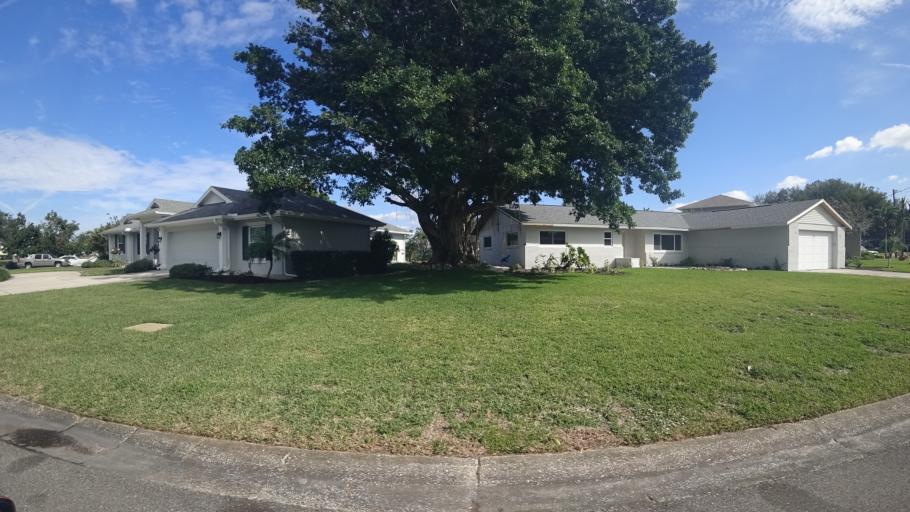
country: US
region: Florida
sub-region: Manatee County
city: West Bradenton
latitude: 27.5168
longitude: -82.6359
